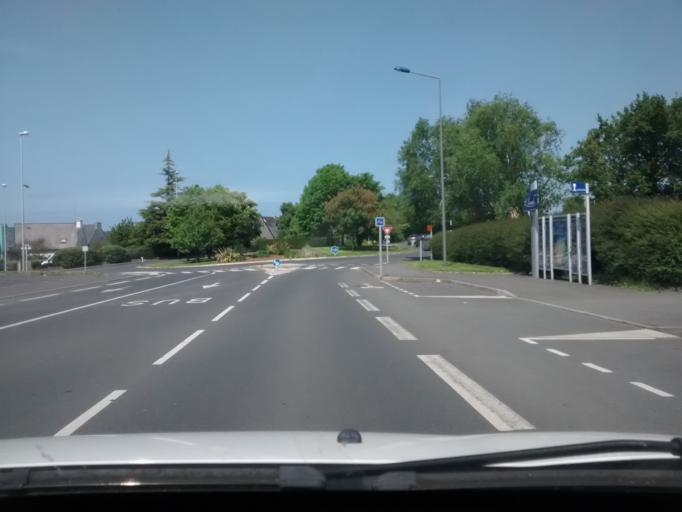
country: FR
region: Brittany
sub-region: Departement des Cotes-d'Armor
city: Langueux
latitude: 48.4999
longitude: -2.7302
